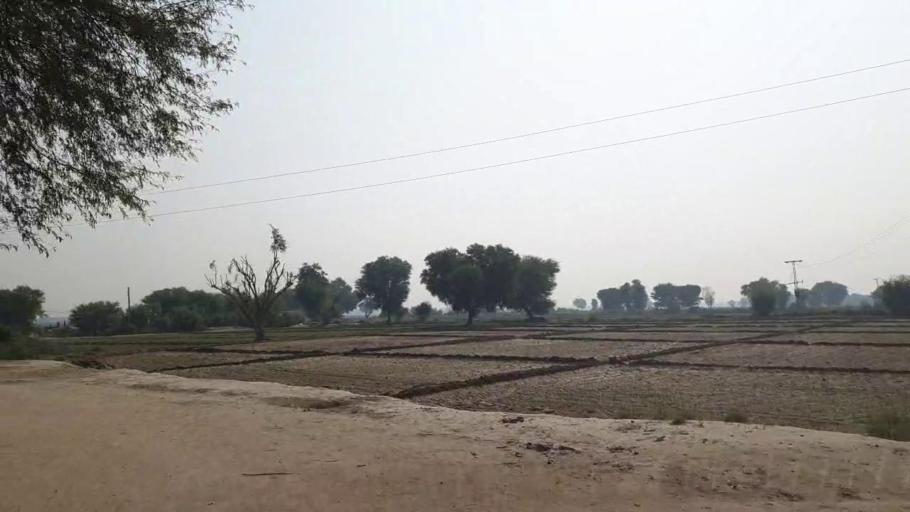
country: PK
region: Sindh
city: Bhan
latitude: 26.5132
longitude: 67.7413
